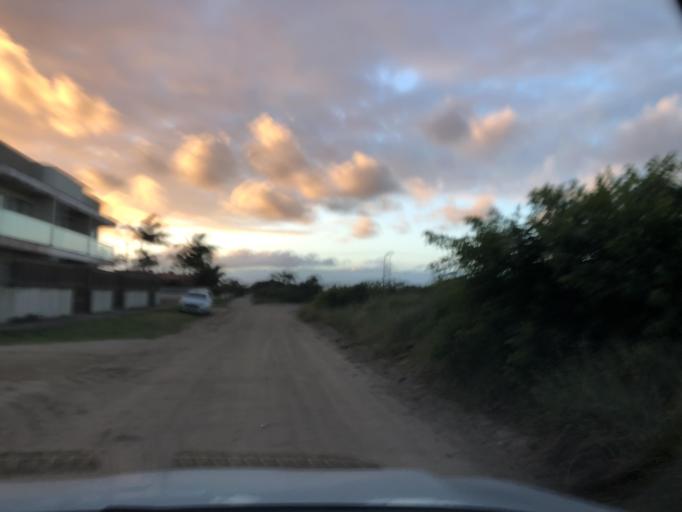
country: BR
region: Santa Catarina
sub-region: Sao Francisco Do Sul
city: Sao Francisco do Sul
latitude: -26.2368
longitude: -48.5107
